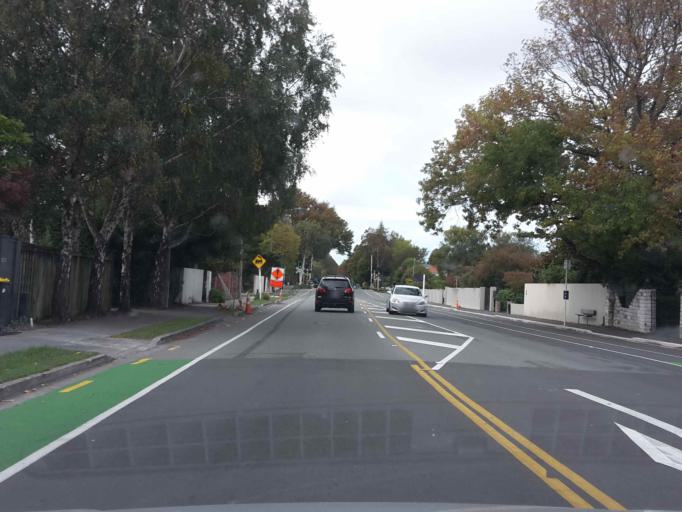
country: NZ
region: Canterbury
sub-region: Christchurch City
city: Christchurch
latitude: -43.5142
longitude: 172.6045
